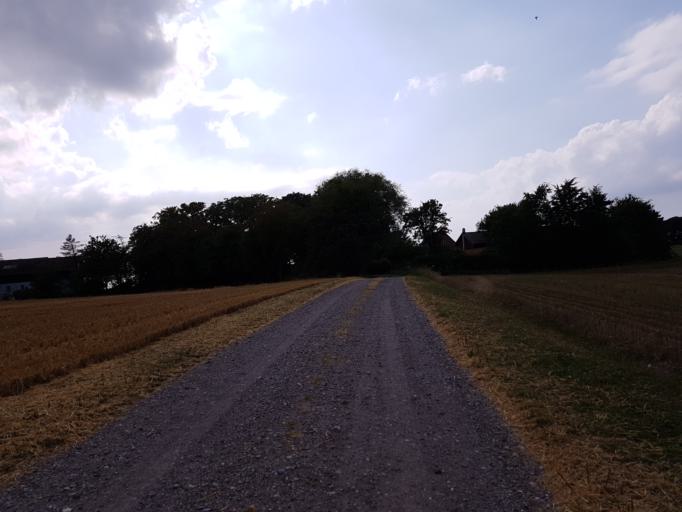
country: DK
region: Zealand
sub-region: Guldborgsund Kommune
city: Nykobing Falster
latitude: 54.6004
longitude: 11.9235
